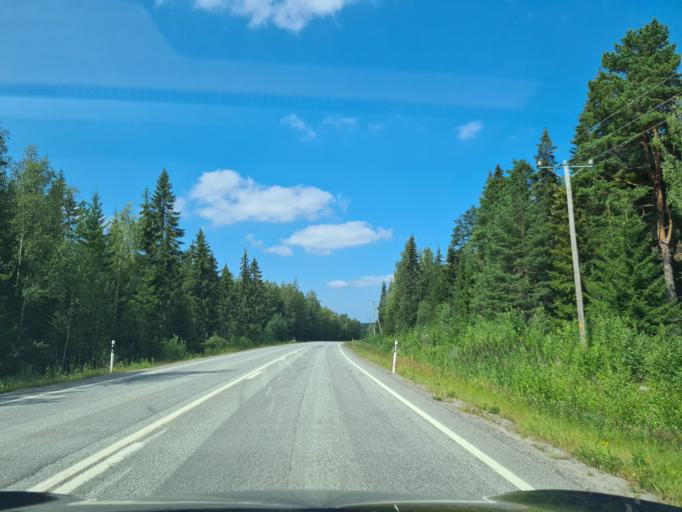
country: FI
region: Ostrobothnia
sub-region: Vaasa
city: Vaasa
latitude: 63.1834
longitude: 21.5690
